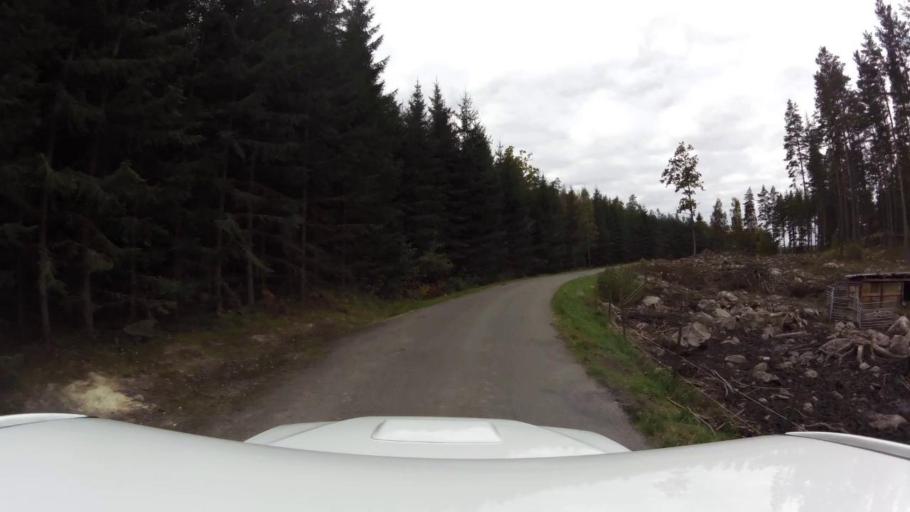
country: SE
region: OEstergoetland
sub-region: Kinda Kommun
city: Rimforsa
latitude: 58.1958
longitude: 15.5830
